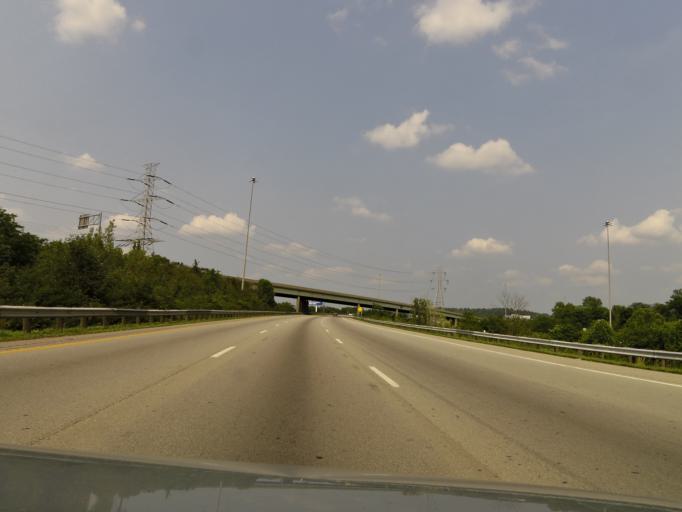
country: US
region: Ohio
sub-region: Hamilton County
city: Lockland
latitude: 39.2095
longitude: -84.4618
